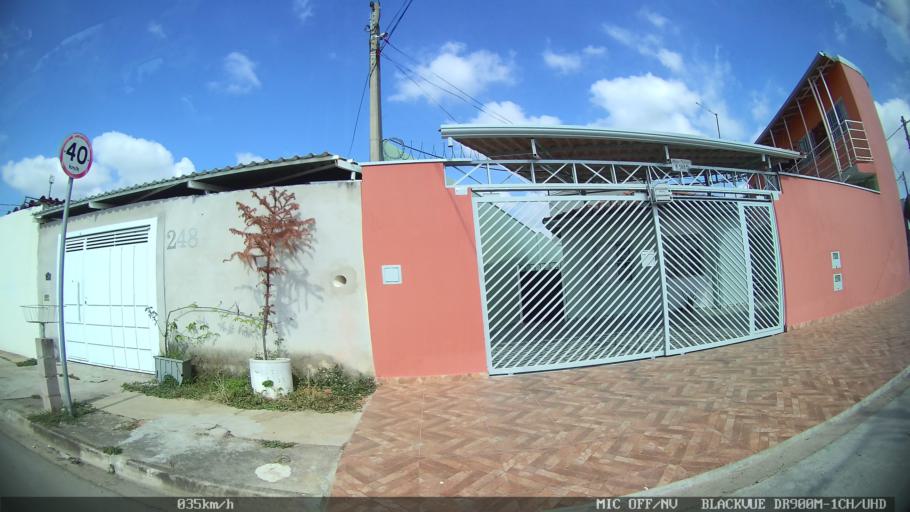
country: BR
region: Sao Paulo
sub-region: Hortolandia
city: Hortolandia
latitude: -22.9696
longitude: -47.1707
